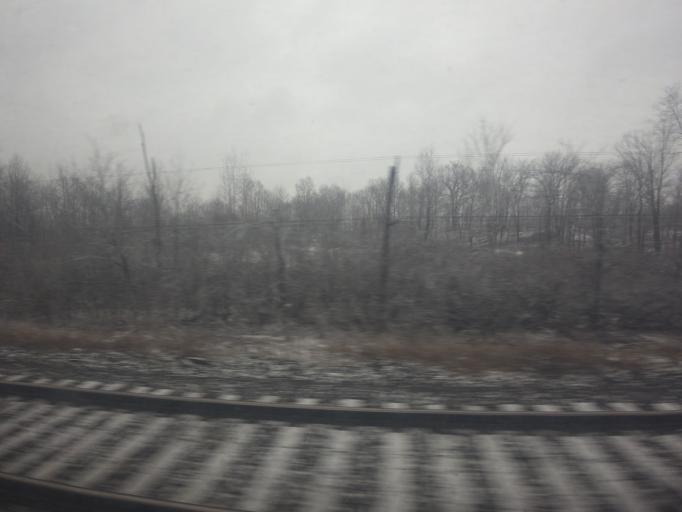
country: US
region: New York
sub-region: Jefferson County
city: Alexandria Bay
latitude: 44.4898
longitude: -75.8743
